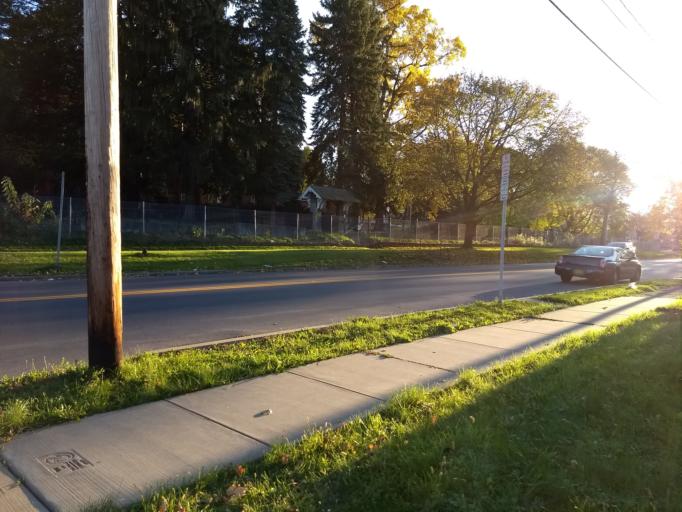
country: US
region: New York
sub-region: Onondaga County
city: Mattydale
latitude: 43.0757
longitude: -76.1521
